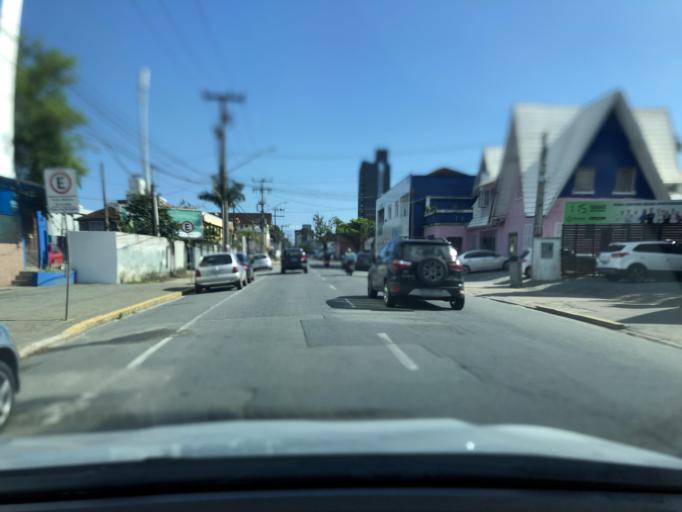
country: BR
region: Santa Catarina
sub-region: Joinville
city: Joinville
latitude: -26.3018
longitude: -48.8421
